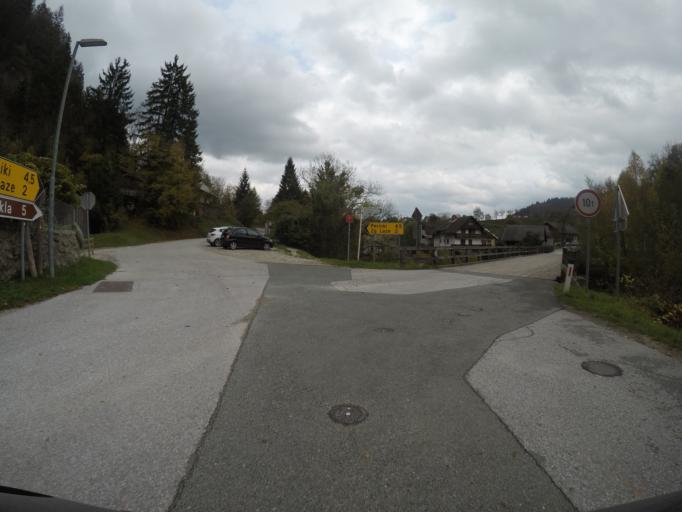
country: SI
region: Gorje
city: Zgornje Gorje
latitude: 46.3785
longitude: 14.0540
